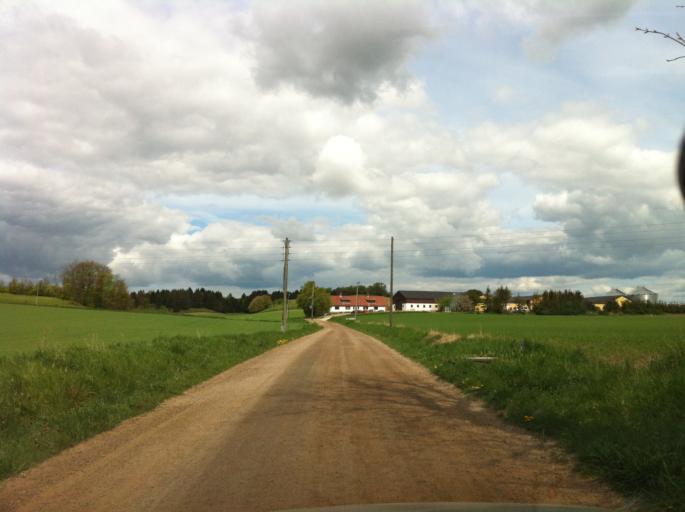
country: SE
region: Skane
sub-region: Svalovs Kommun
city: Teckomatorp
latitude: 55.8233
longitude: 13.0677
